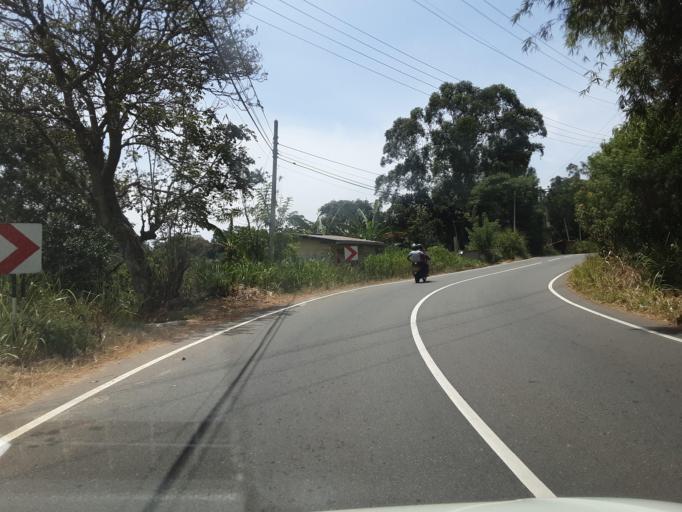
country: LK
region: Central
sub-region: Nuwara Eliya District
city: Nuwara Eliya
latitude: 6.9345
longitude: 80.9069
